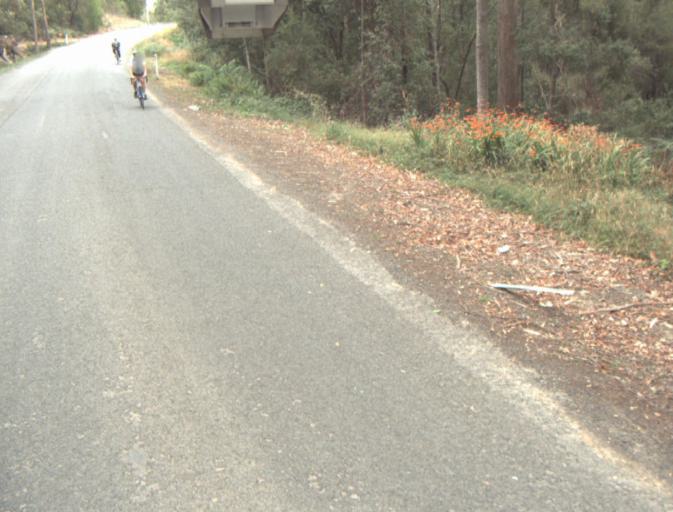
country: AU
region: Tasmania
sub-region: Launceston
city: Mayfield
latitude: -41.2143
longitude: 147.2116
